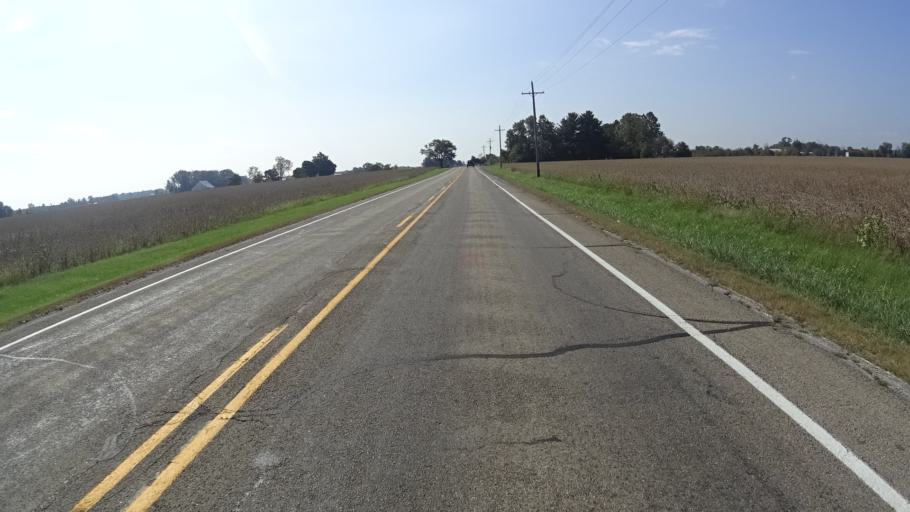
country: US
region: Indiana
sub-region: Madison County
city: Lapel
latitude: 40.0135
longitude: -85.8432
